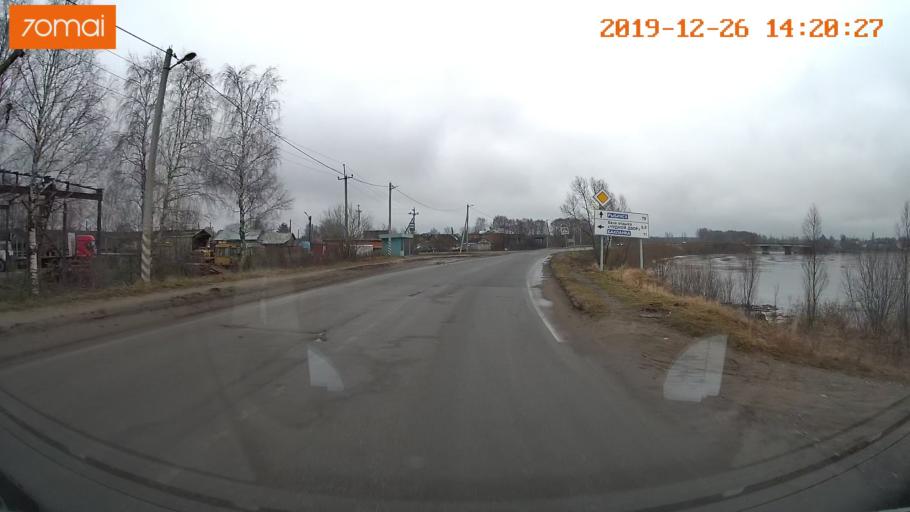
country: RU
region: Jaroslavl
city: Poshekhon'ye
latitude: 58.5097
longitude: 39.1303
